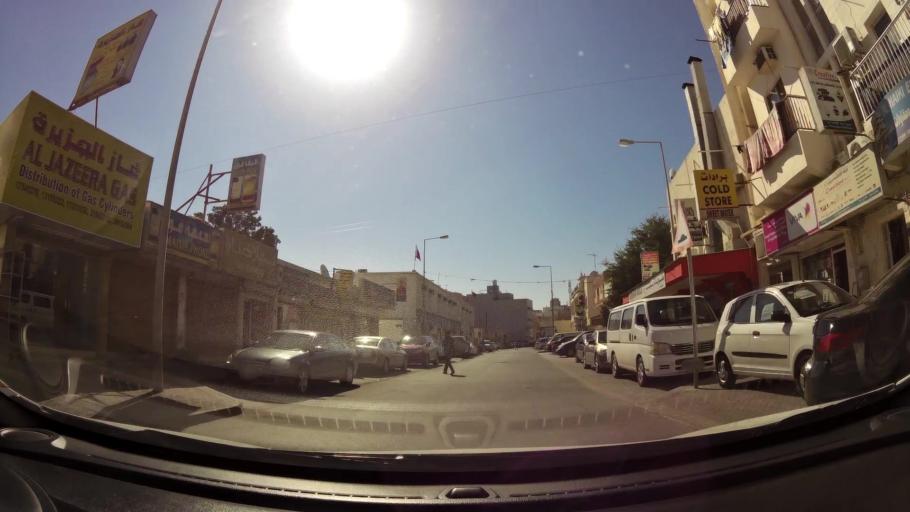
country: BH
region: Muharraq
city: Al Muharraq
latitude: 26.2554
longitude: 50.6175
